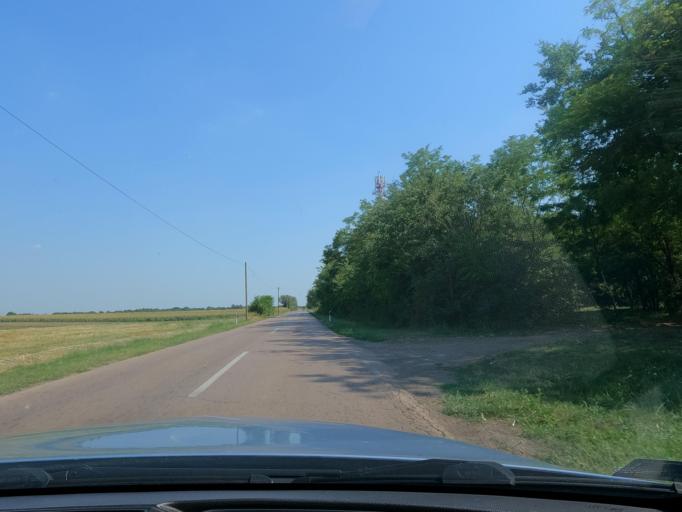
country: RS
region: Autonomna Pokrajina Vojvodina
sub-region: Severnobacki Okrug
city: Mali Igos
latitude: 45.7696
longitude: 19.7360
